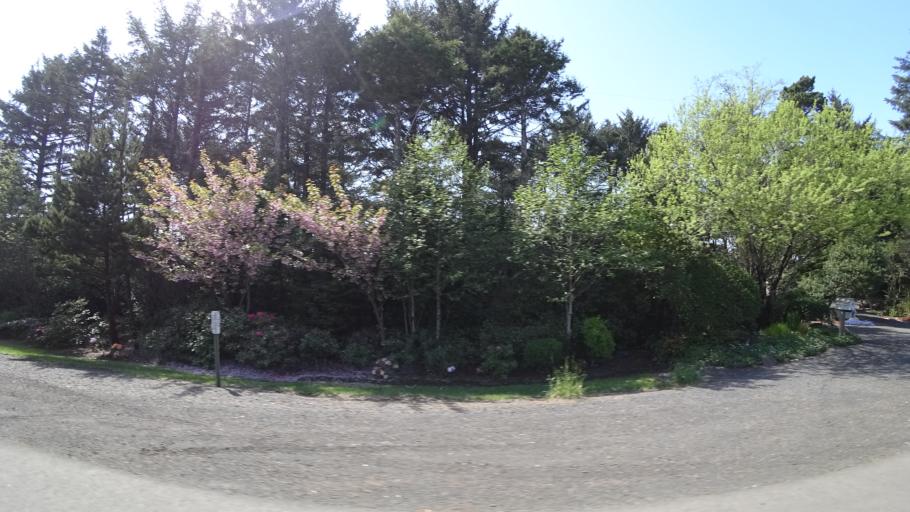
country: US
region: Oregon
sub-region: Lincoln County
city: Newport
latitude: 44.6915
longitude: -124.0633
